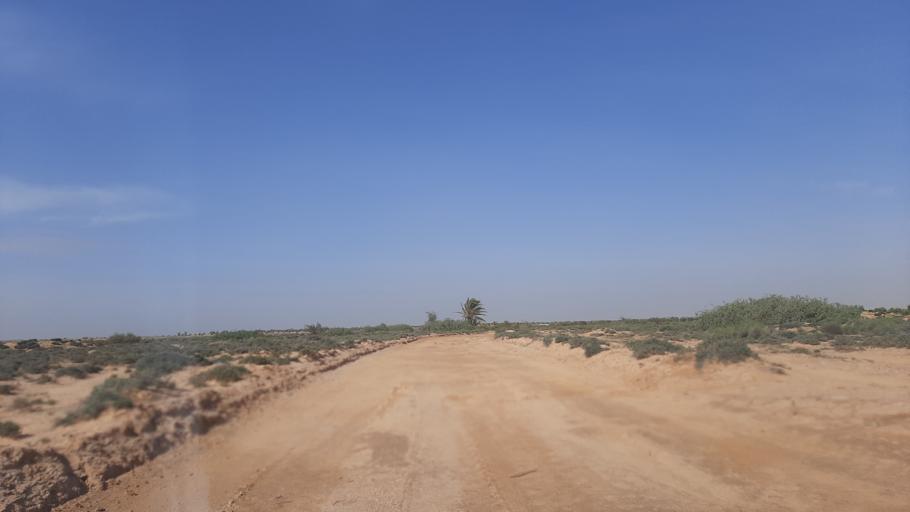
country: TN
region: Madanin
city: Zarzis
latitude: 33.4446
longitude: 10.8083
